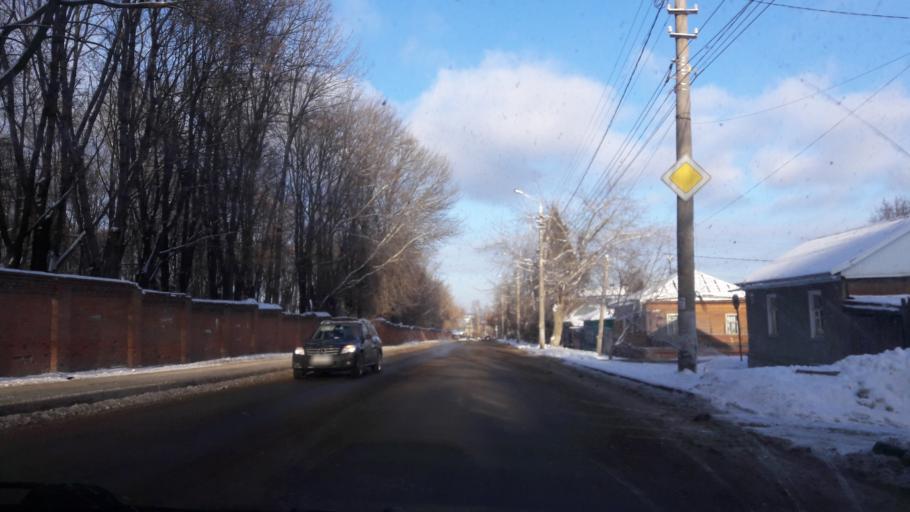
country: RU
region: Tula
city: Tula
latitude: 54.1780
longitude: 37.6149
